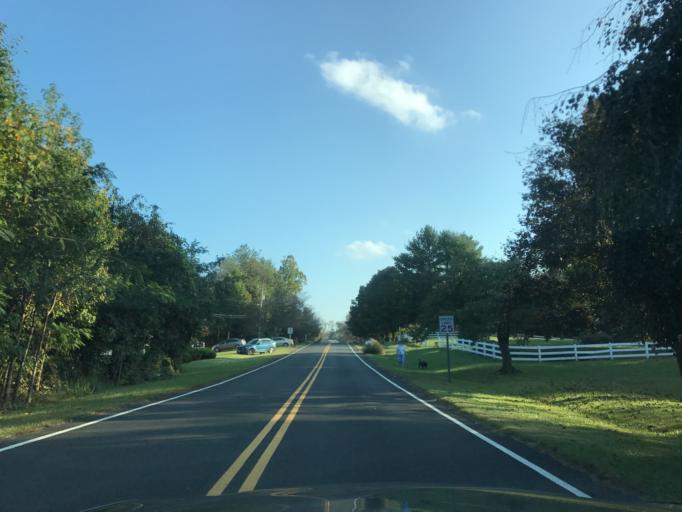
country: US
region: Maryland
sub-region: Anne Arundel County
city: Crownsville
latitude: 39.0436
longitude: -76.6188
